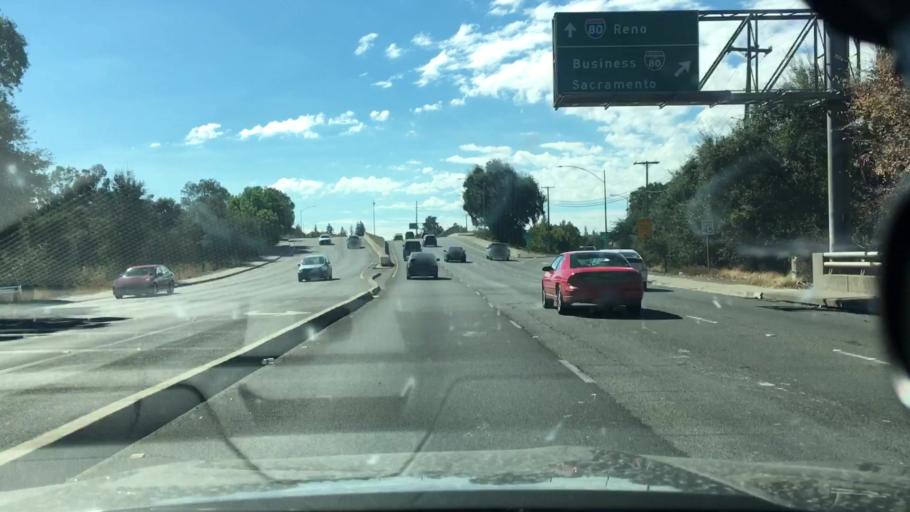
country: US
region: California
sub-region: Sacramento County
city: Arden-Arcade
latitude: 38.6418
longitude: -121.3833
